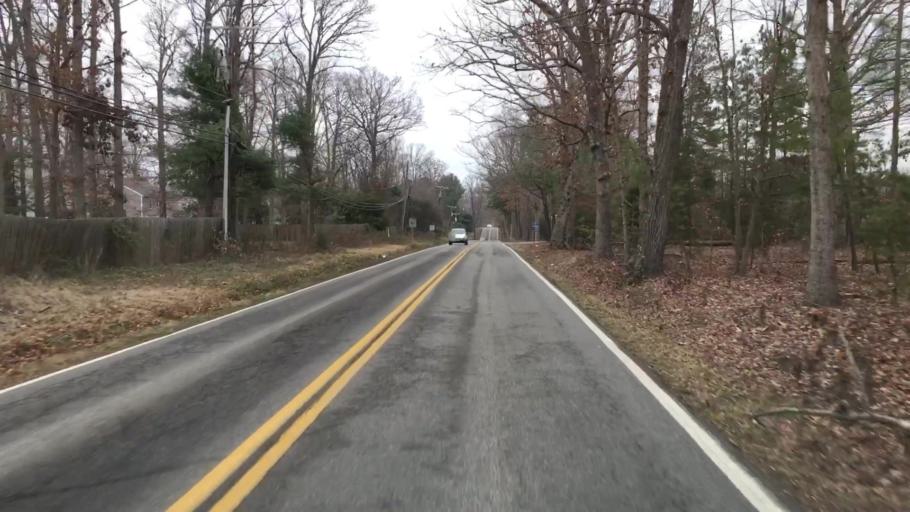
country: US
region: Virginia
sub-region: Chesterfield County
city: Bon Air
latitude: 37.5170
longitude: -77.5748
